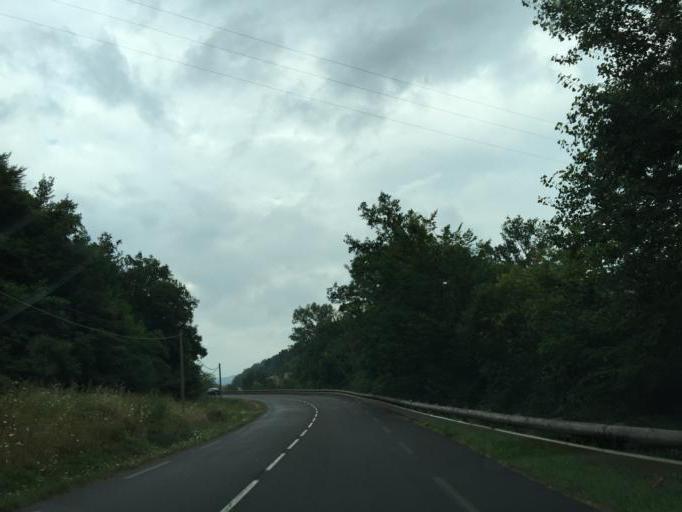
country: FR
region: Rhone-Alpes
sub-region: Departement de la Loire
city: Sorbiers
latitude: 45.5065
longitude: 4.4383
